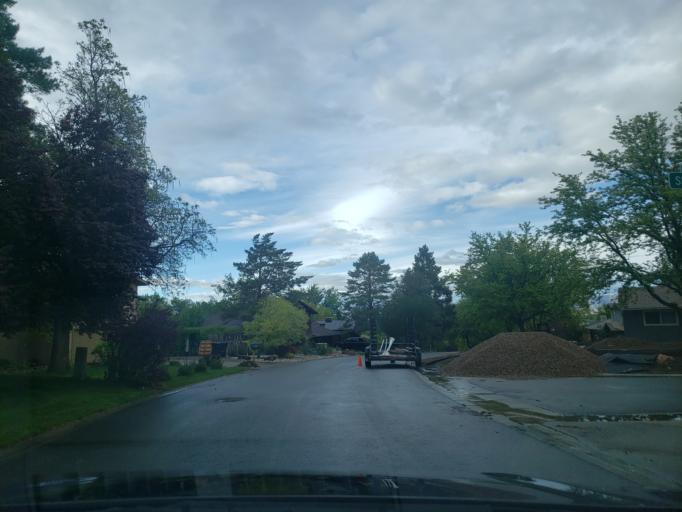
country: US
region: Colorado
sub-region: Mesa County
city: Redlands
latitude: 39.0952
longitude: -108.6525
